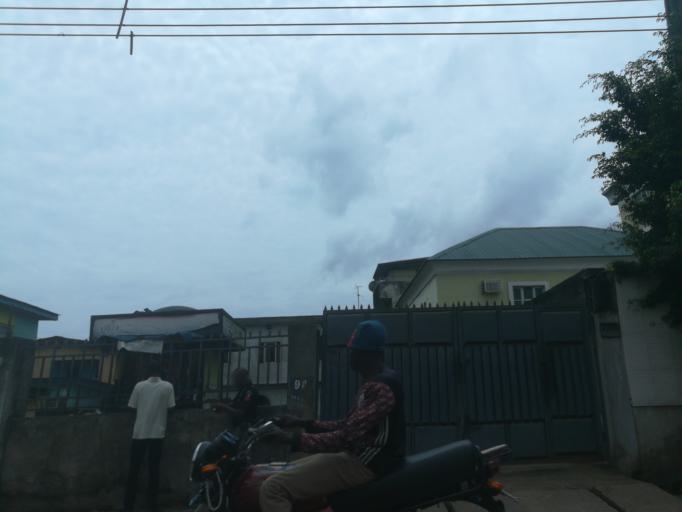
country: NG
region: Lagos
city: Somolu
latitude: 6.5312
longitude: 3.3881
